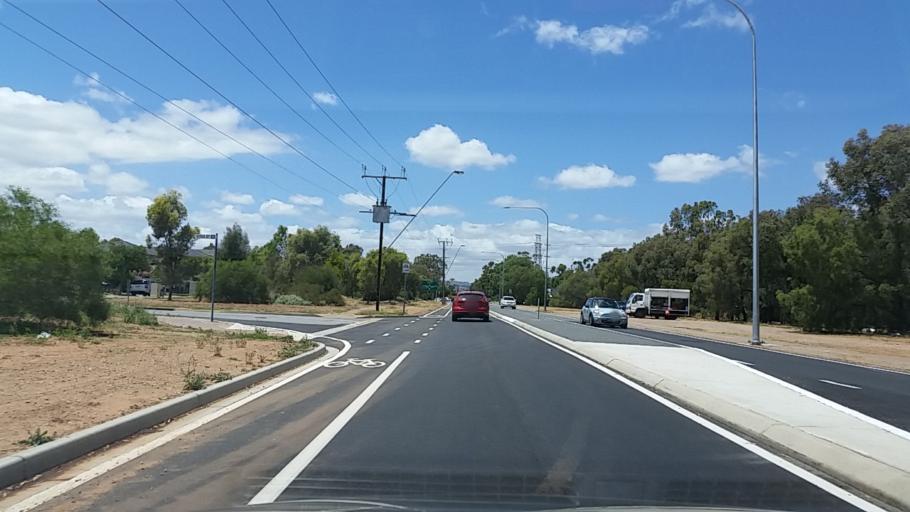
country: AU
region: South Australia
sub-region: Salisbury
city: Salisbury
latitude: -34.7713
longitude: 138.6134
